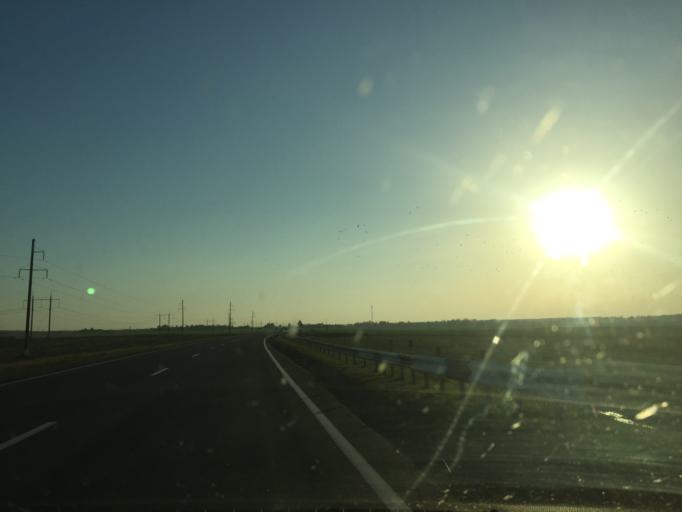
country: BY
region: Mogilev
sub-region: Mahilyowski Rayon
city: Kadino
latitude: 53.8273
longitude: 30.4746
